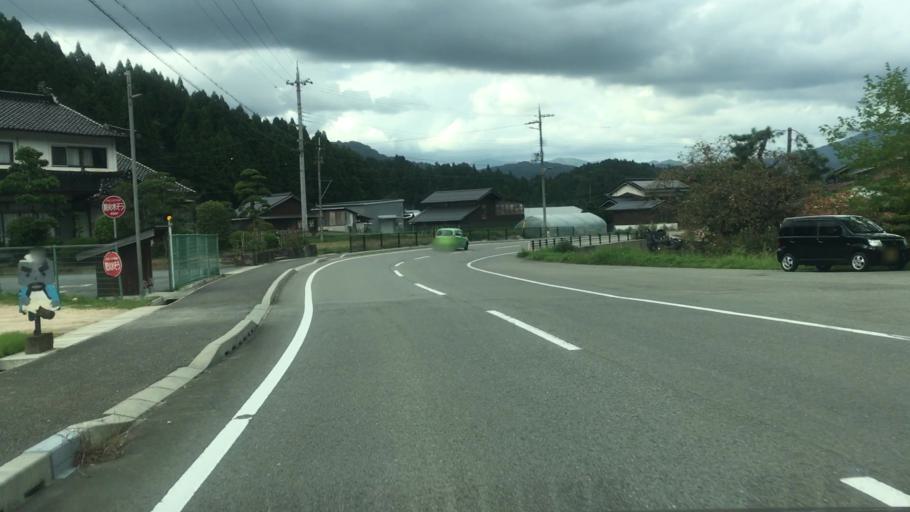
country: JP
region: Hyogo
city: Toyooka
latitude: 35.4392
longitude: 134.7329
